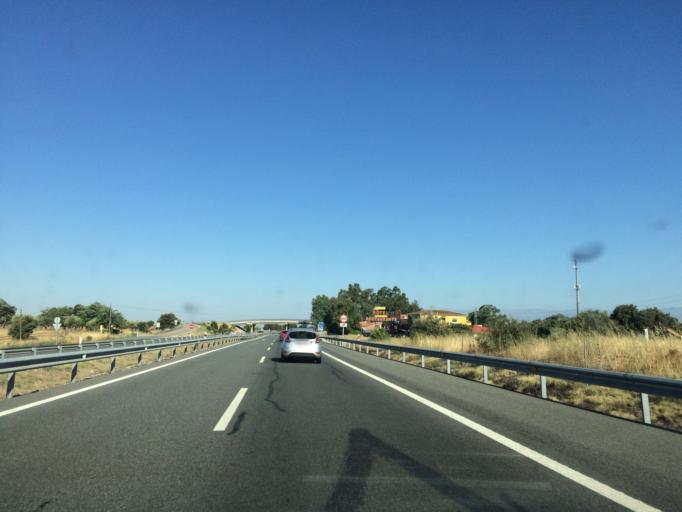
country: ES
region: Castille-La Mancha
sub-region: Province of Toledo
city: Alcanizo
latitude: 39.9181
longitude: -5.0781
